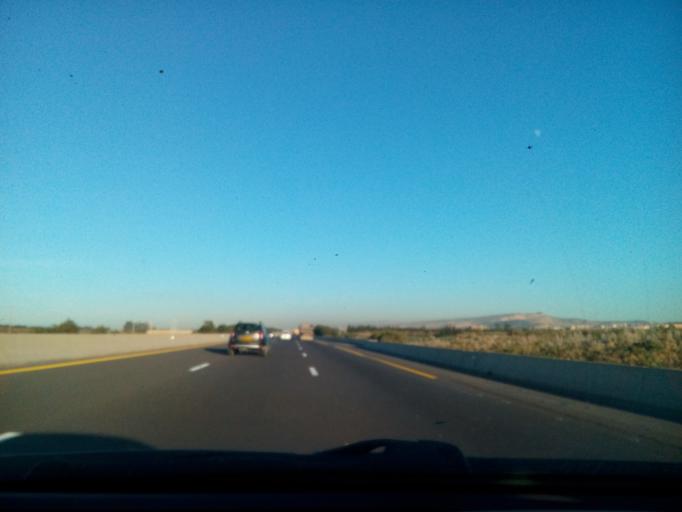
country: DZ
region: Relizane
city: Djidiouia
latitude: 35.9323
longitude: 0.8094
